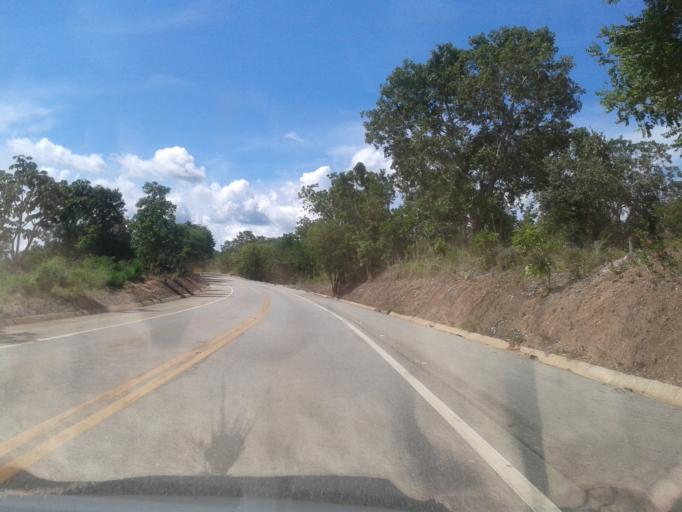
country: BR
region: Goias
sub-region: Goias
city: Goias
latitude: -15.6765
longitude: -50.2091
